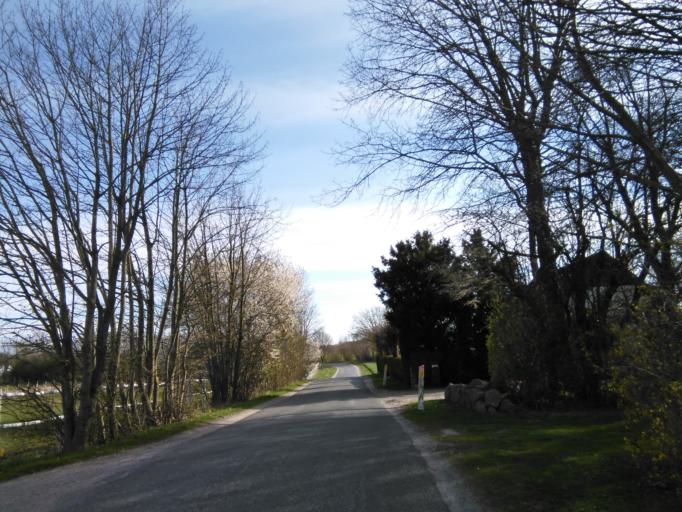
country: DK
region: Central Jutland
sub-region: Arhus Kommune
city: Marslet
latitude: 56.0537
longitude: 10.1655
